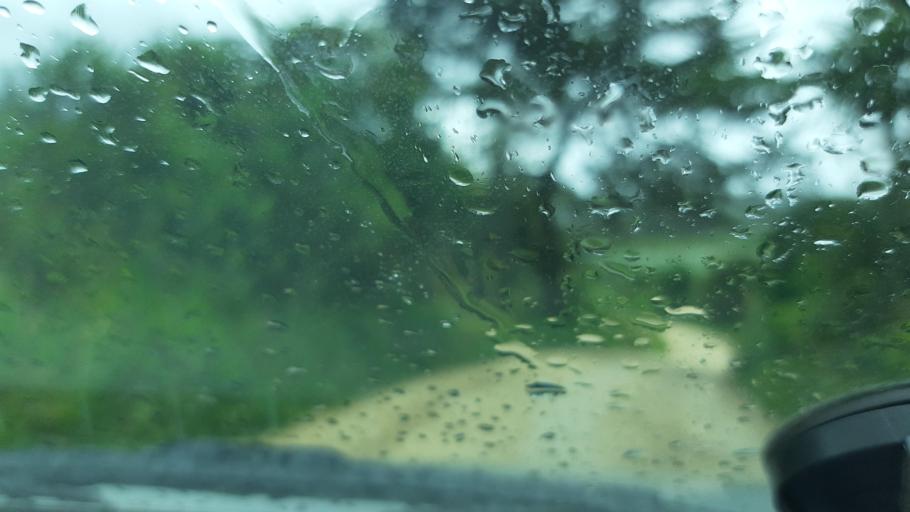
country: CO
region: Cundinamarca
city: Umbita
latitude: 5.2493
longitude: -73.4657
